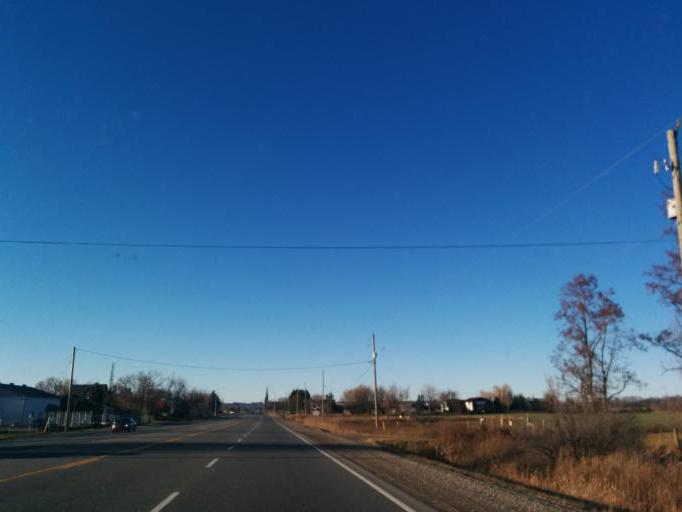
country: CA
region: Ontario
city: Brampton
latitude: 43.7914
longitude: -79.9025
